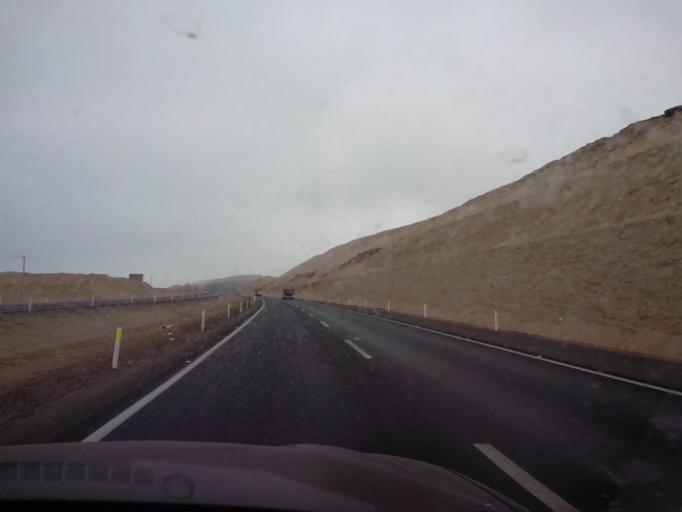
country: PE
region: Ica
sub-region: Provincia de Chincha
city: San Pedro
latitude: -13.3095
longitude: -76.2501
